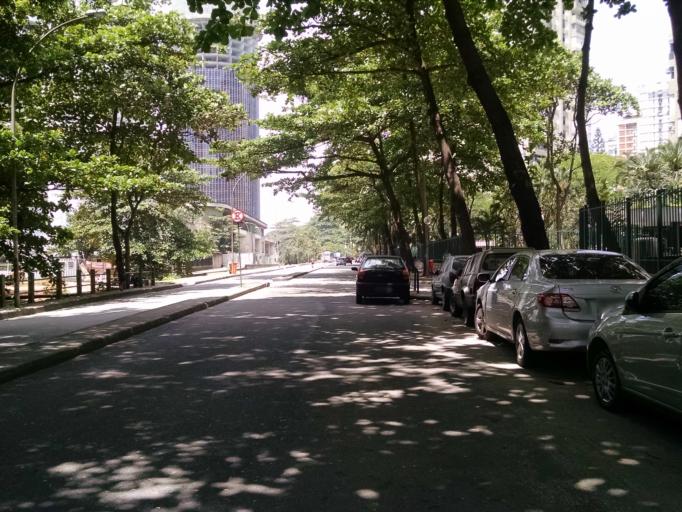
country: BR
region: Rio de Janeiro
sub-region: Rio De Janeiro
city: Rio de Janeiro
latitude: -22.9956
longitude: -43.2556
